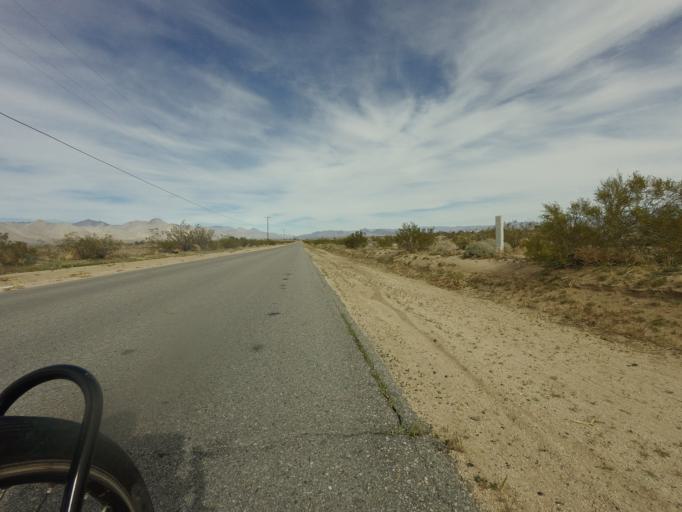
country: US
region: California
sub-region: Kern County
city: Inyokern
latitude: 35.6968
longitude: -117.8271
